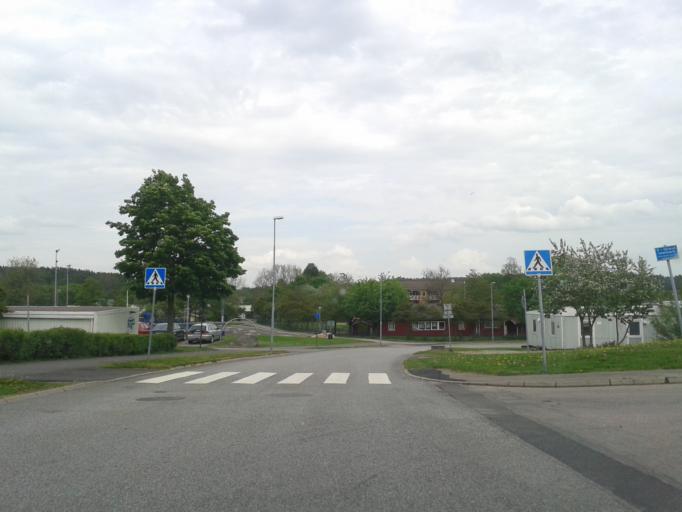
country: SE
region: Vaestra Goetaland
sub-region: Kungalvs Kommun
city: Kungalv
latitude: 57.8849
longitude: 11.9601
